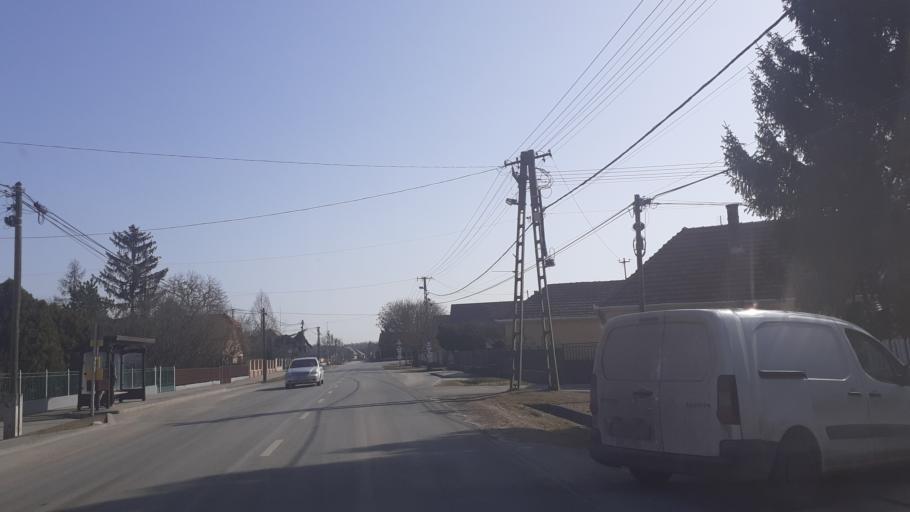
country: HU
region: Pest
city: Dabas
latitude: 47.1654
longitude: 19.3315
